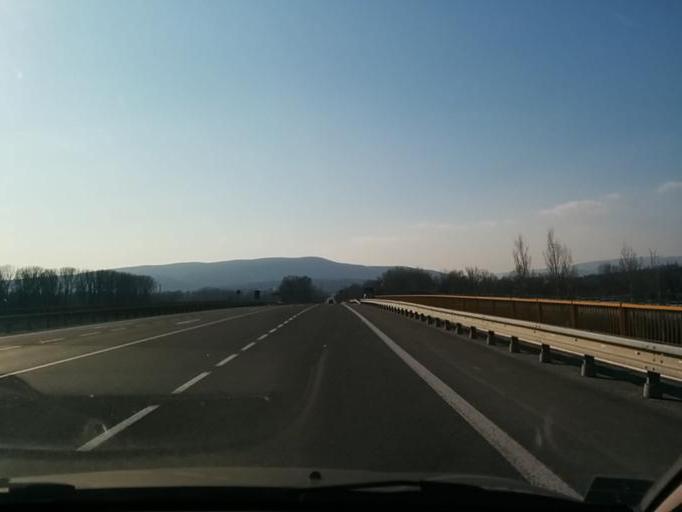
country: SK
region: Trenciansky
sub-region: Okres Nove Mesto nad Vahom
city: Nove Mesto nad Vahom
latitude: 48.7621
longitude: 17.8682
